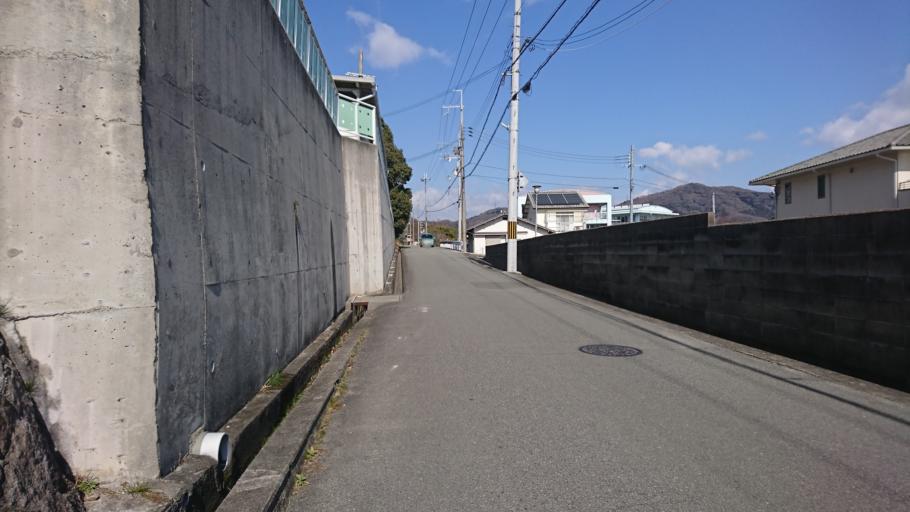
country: JP
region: Hyogo
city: Kakogawacho-honmachi
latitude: 34.8149
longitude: 134.8034
